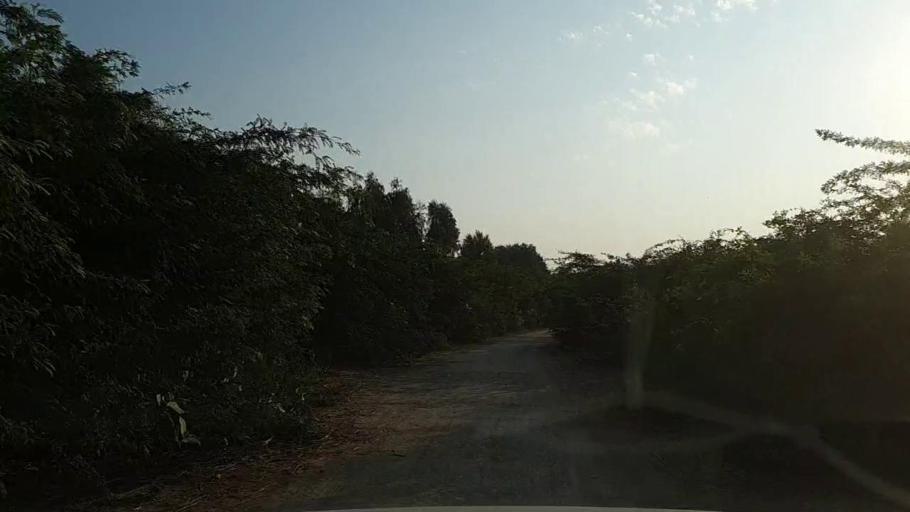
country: PK
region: Sindh
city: Daro Mehar
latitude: 24.7651
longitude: 68.1929
